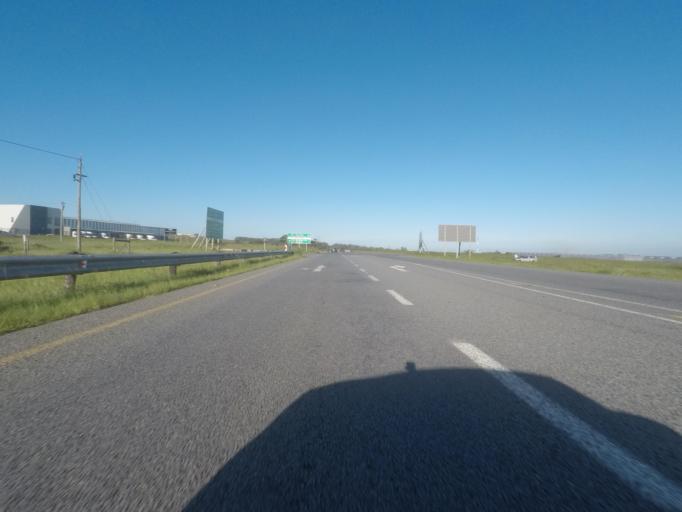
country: ZA
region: Eastern Cape
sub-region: Buffalo City Metropolitan Municipality
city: East London
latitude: -33.0527
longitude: 27.8084
